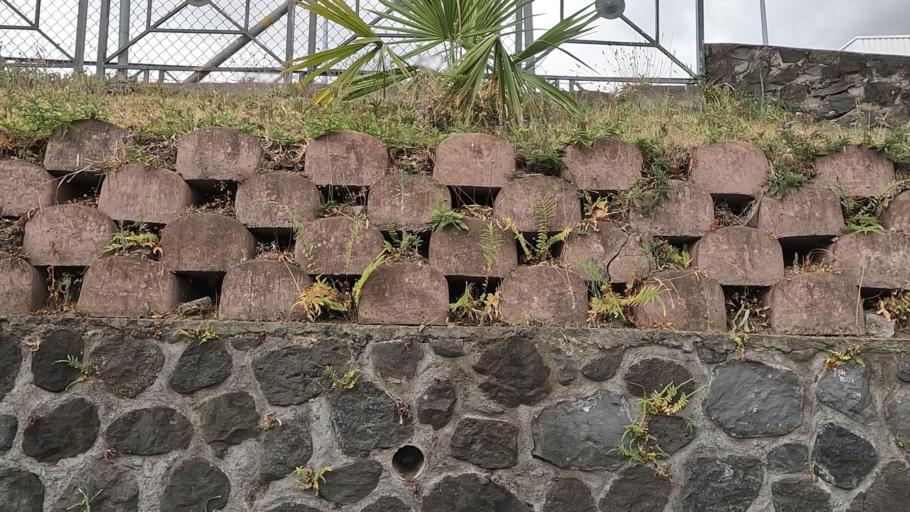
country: RE
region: Reunion
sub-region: Reunion
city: Le Tampon
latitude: -21.2783
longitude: 55.5054
